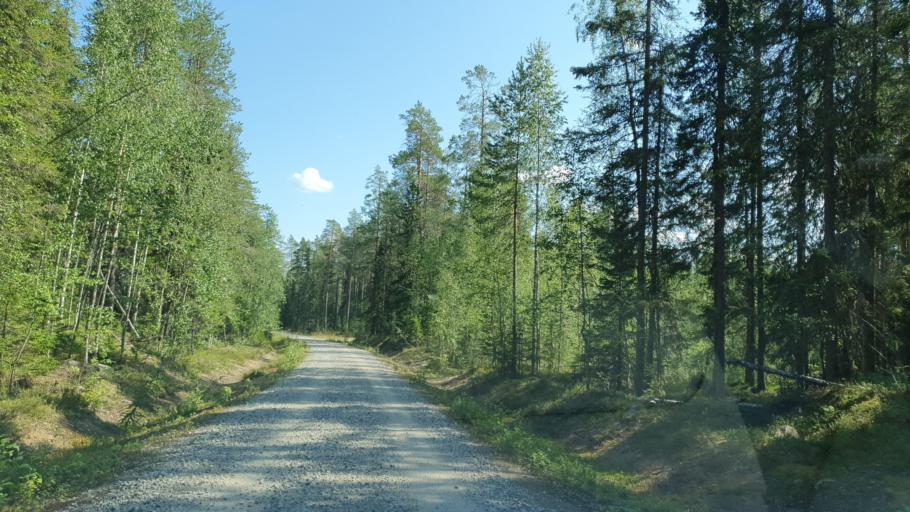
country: FI
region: Kainuu
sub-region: Kehys-Kainuu
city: Kuhmo
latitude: 63.9656
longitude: 29.5422
